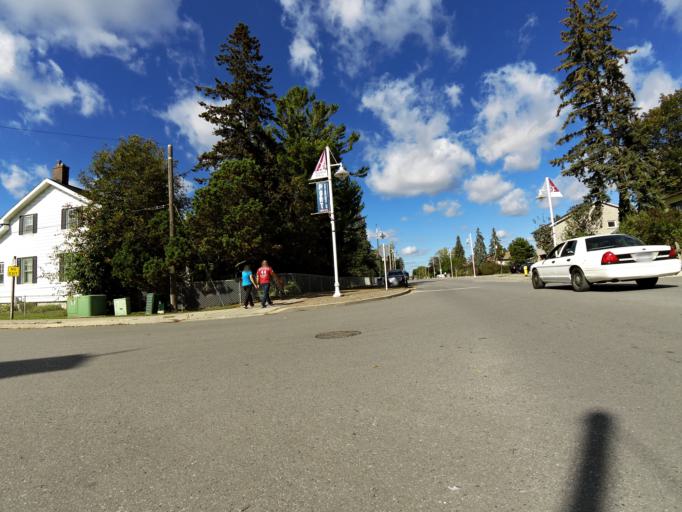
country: CA
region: Ontario
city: Ajax
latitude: 43.8160
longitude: -79.0818
